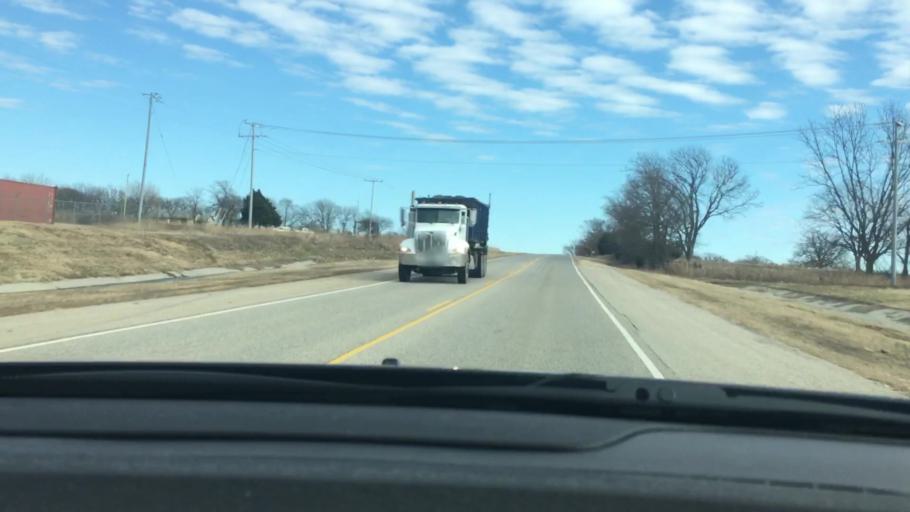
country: US
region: Oklahoma
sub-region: Garvin County
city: Stratford
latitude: 34.7968
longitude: -96.8564
